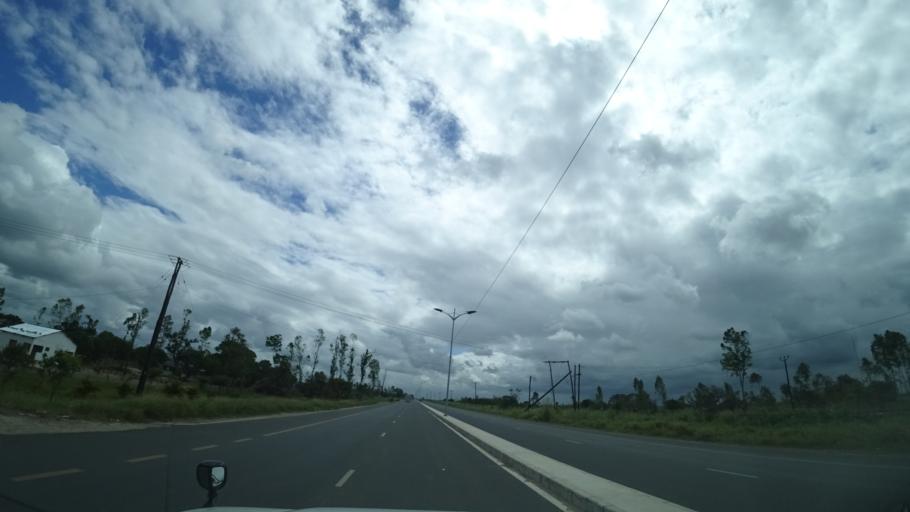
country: MZ
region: Sofala
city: Dondo
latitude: -19.5890
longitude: 34.7368
